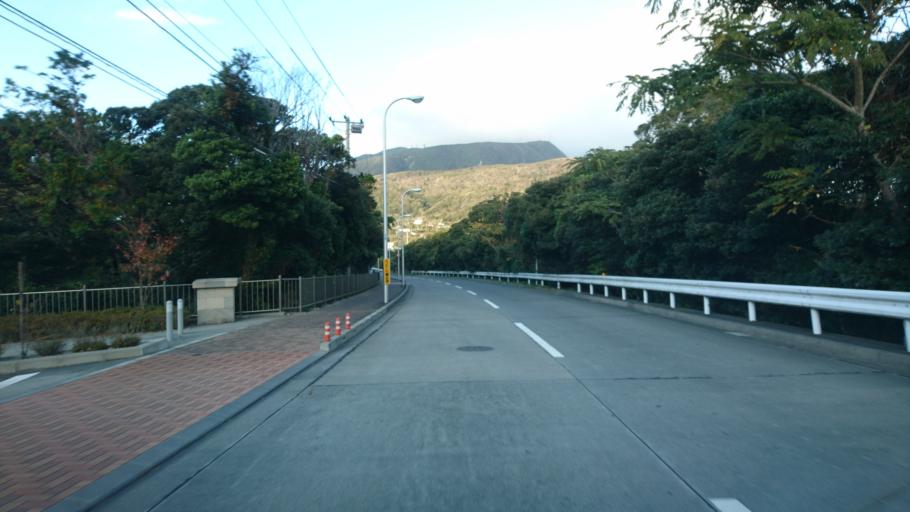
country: JP
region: Shizuoka
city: Shimoda
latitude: 34.3684
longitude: 139.2589
